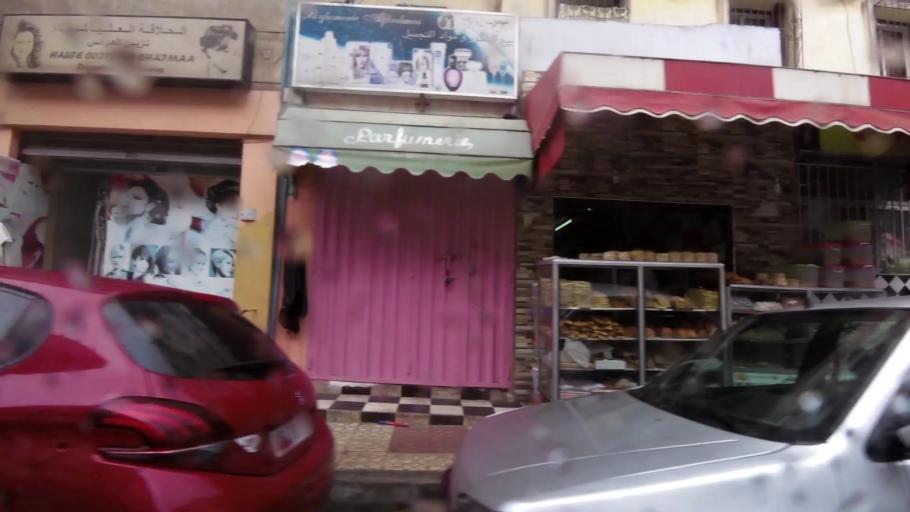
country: MA
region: Grand Casablanca
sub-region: Casablanca
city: Casablanca
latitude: 33.6008
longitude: -7.6369
